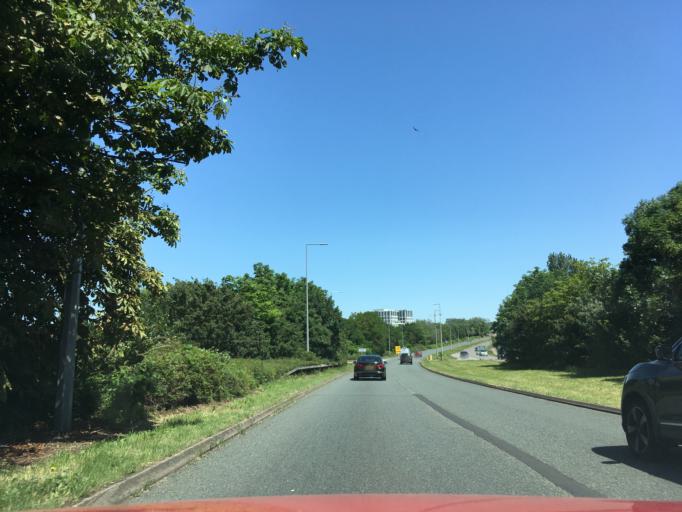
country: GB
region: England
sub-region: Milton Keynes
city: Loughton
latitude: 52.0271
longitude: -0.7749
